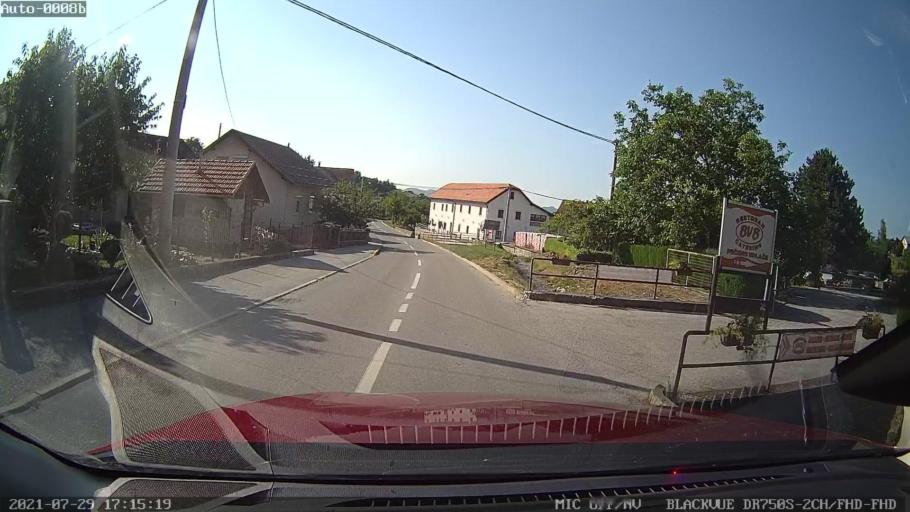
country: HR
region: Varazdinska
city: Ivanec
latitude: 46.2111
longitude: 16.1312
